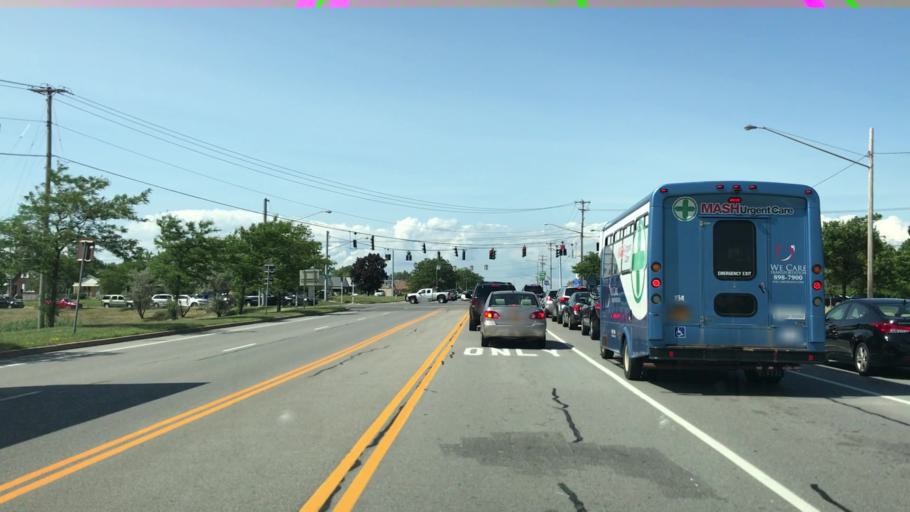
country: US
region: New York
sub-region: Erie County
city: Sloan
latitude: 42.9063
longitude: -78.7841
